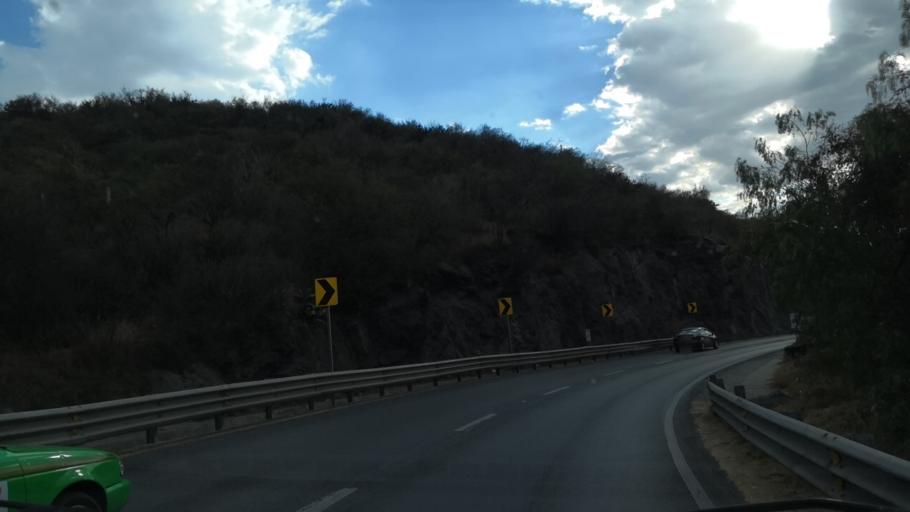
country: MX
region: Guanajuato
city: Marfil
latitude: 21.0012
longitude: -101.2819
